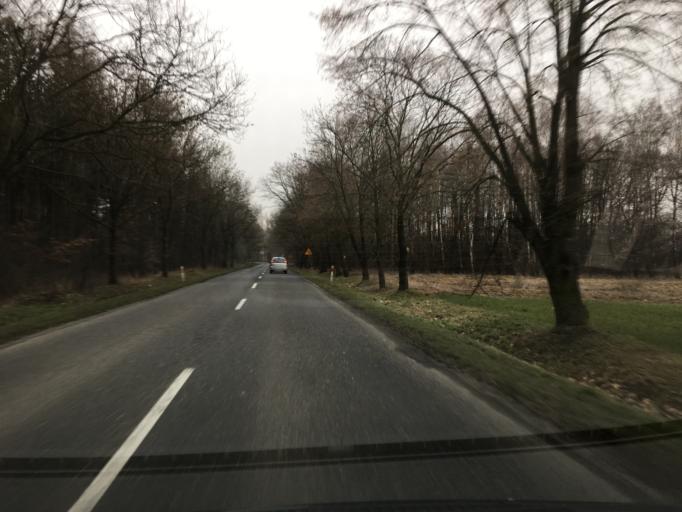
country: PL
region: Opole Voivodeship
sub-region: Powiat kedzierzynsko-kozielski
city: Bierawa
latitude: 50.3000
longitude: 18.2319
